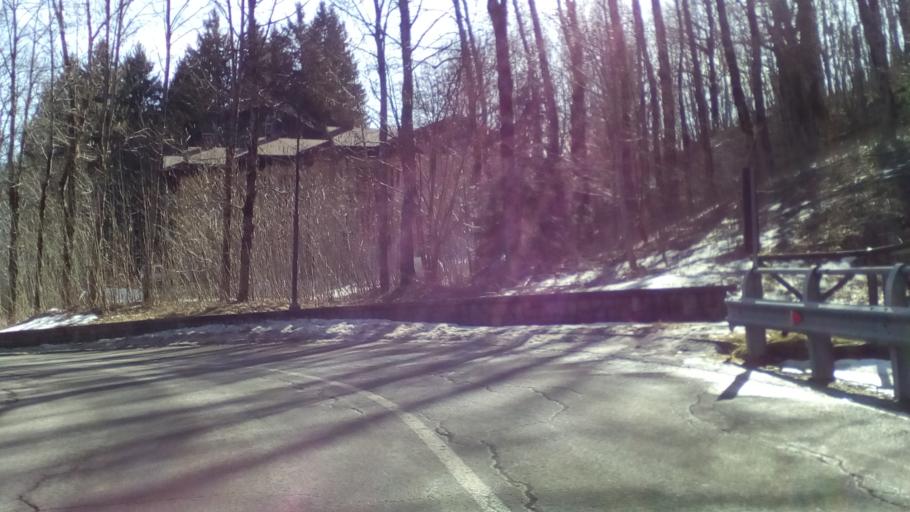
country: IT
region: Emilia-Romagna
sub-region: Provincia di Modena
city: Pievepelago
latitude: 44.1918
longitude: 10.5494
